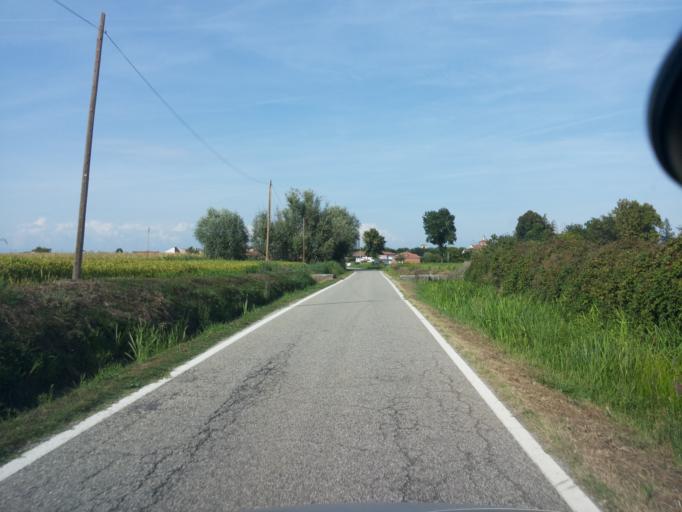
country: IT
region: Piedmont
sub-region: Provincia di Vercelli
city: San Germano Vercellese
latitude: 45.3459
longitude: 8.2435
